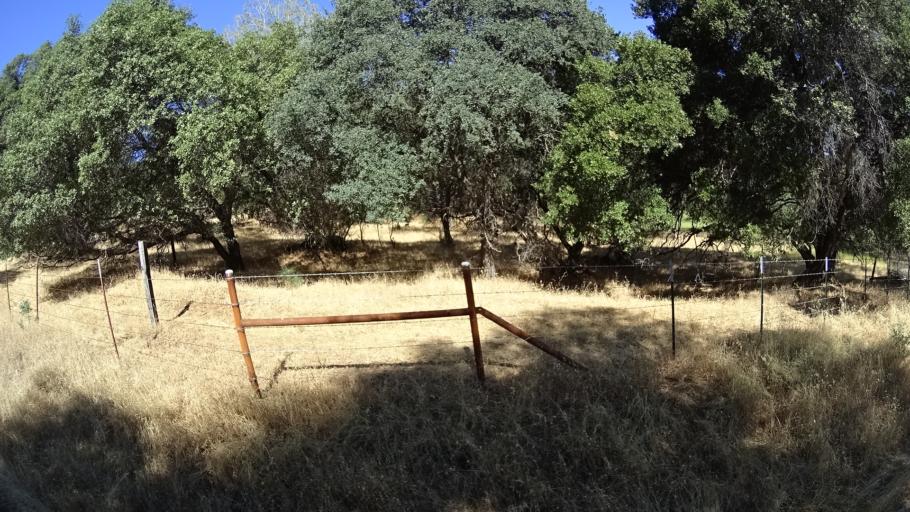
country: US
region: California
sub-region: Calaveras County
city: Murphys
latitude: 38.0835
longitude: -120.4759
